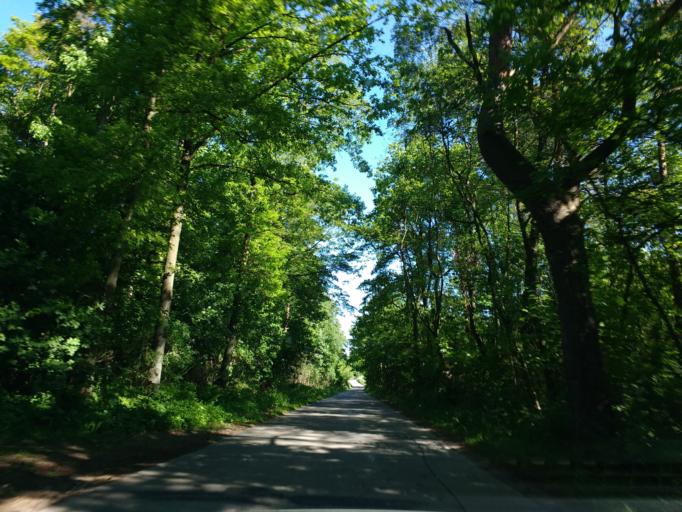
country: DE
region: Mecklenburg-Vorpommern
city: Neukloster
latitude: 53.8548
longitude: 11.6799
